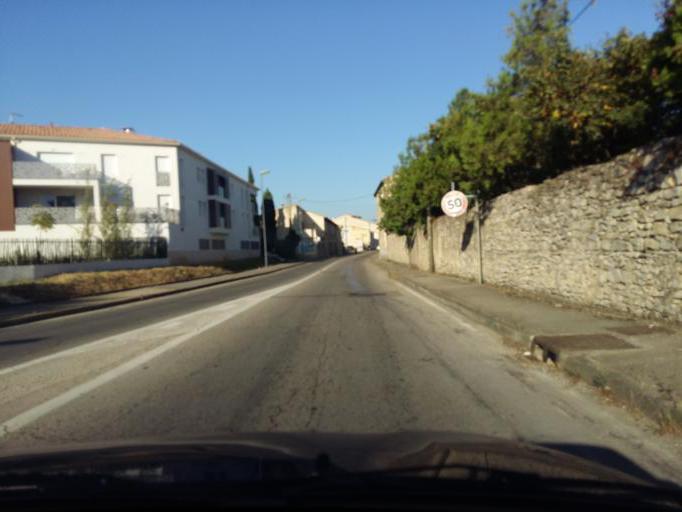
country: FR
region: Languedoc-Roussillon
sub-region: Departement du Gard
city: Saint-Gervasy
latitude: 43.8752
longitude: 4.4668
